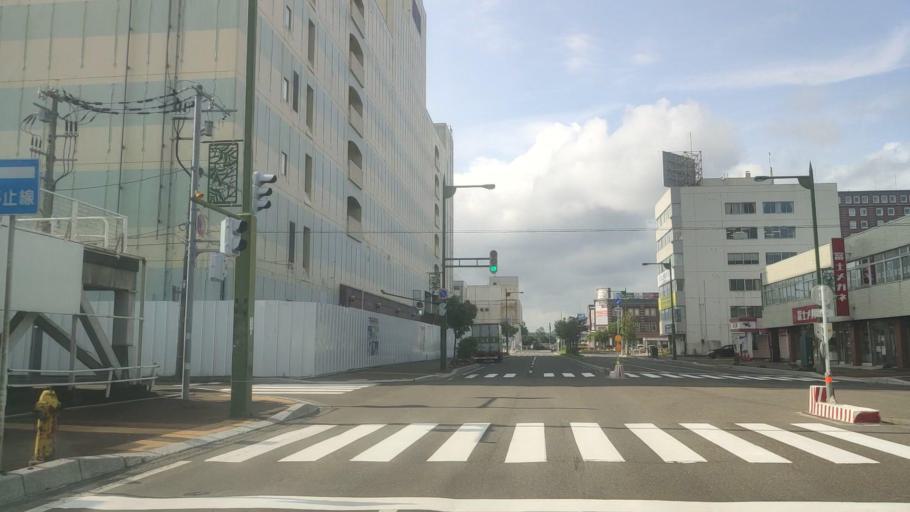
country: JP
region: Hokkaido
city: Tomakomai
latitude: 42.6381
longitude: 141.5984
